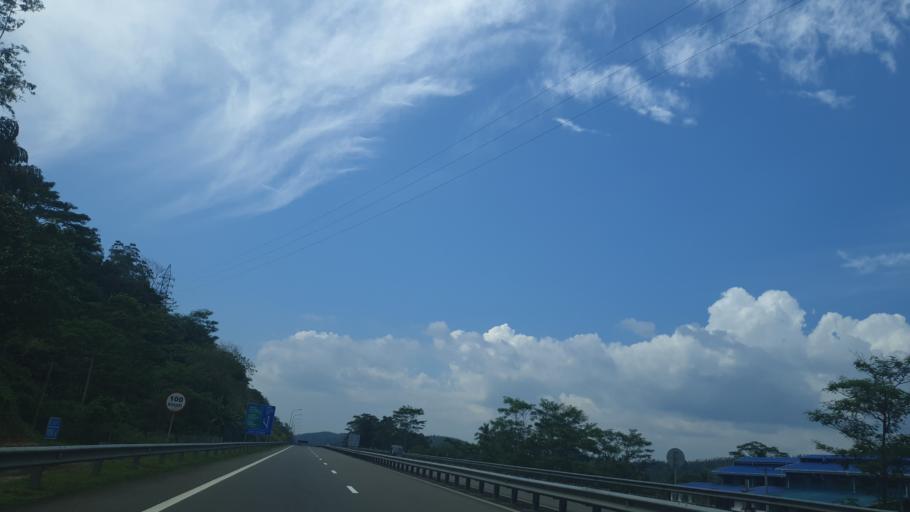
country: LK
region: Southern
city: Weligama
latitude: 6.0330
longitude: 80.3742
